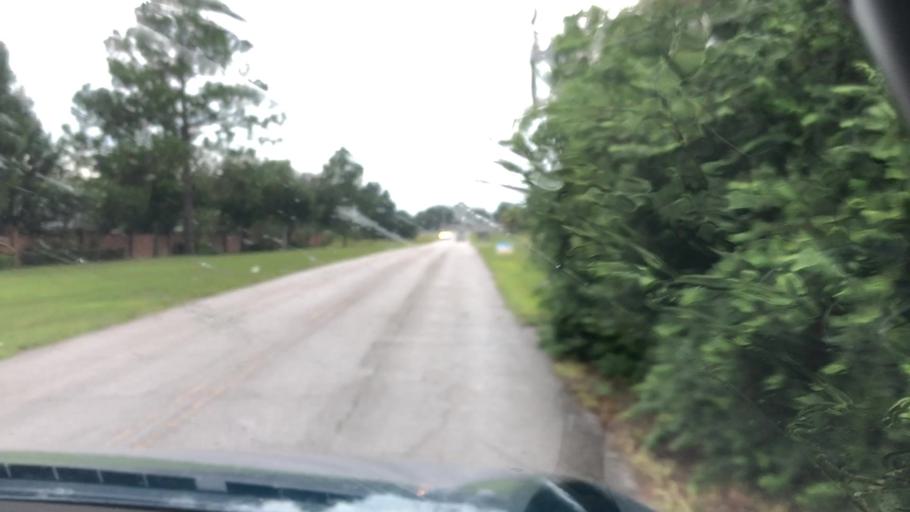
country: US
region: Florida
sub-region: Lake County
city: Eustis
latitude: 28.8793
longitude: -81.7371
